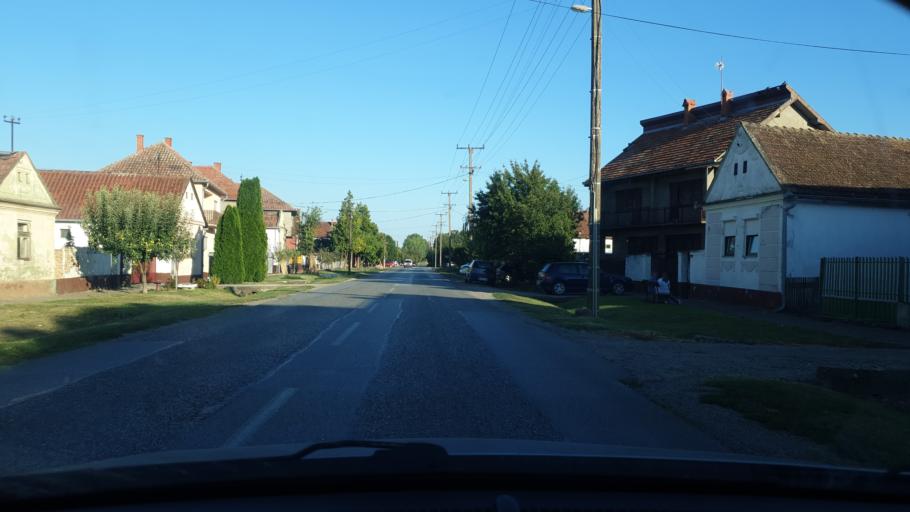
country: RS
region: Autonomna Pokrajina Vojvodina
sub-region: Sremski Okrug
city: Ruma
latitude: 44.9758
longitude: 19.8874
